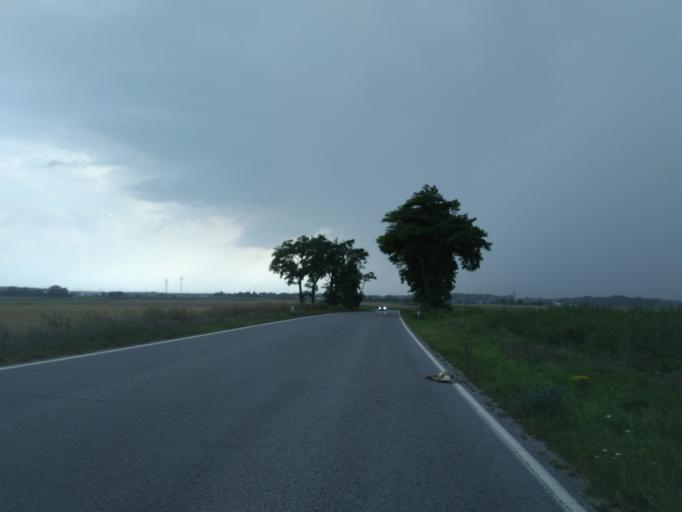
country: AT
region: Lower Austria
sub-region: Politischer Bezirk Ganserndorf
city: Ganserndorf
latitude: 48.3747
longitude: 16.7179
